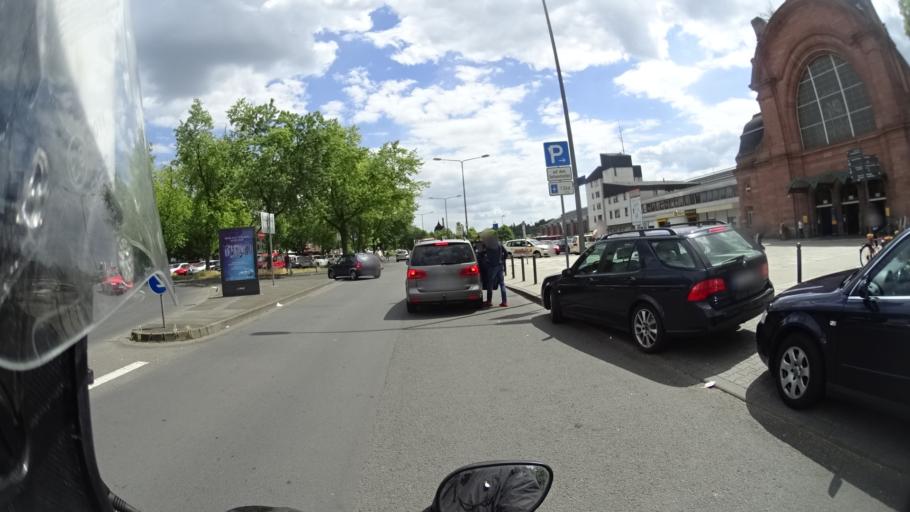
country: DE
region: Hesse
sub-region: Regierungsbezirk Darmstadt
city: Wiesbaden
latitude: 50.0712
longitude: 8.2449
